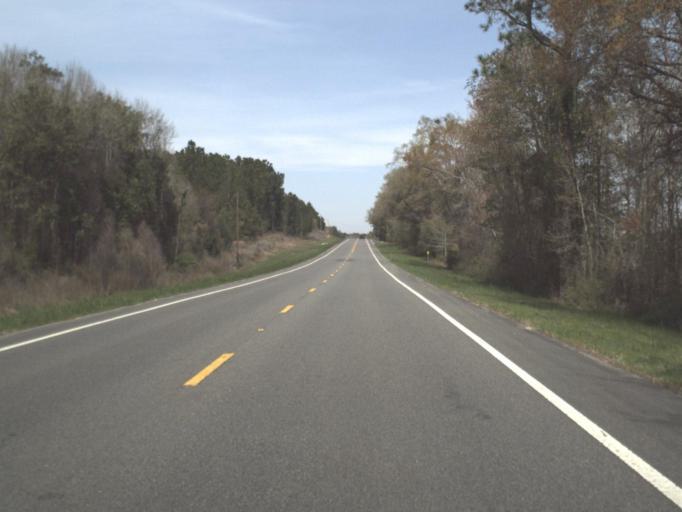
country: US
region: Florida
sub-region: Walton County
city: DeFuniak Springs
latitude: 30.8088
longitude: -85.9583
